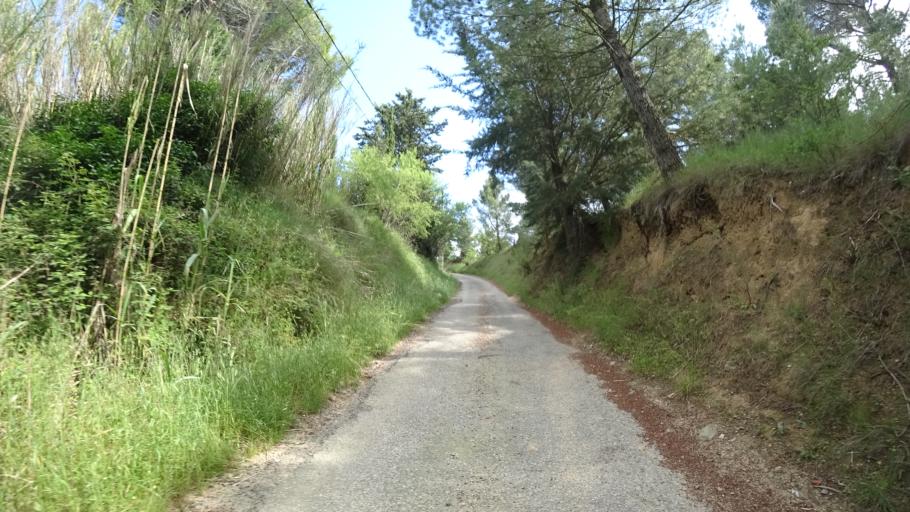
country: FR
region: Languedoc-Roussillon
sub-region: Departement de l'Aude
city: Ginestas
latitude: 43.2640
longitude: 2.8741
